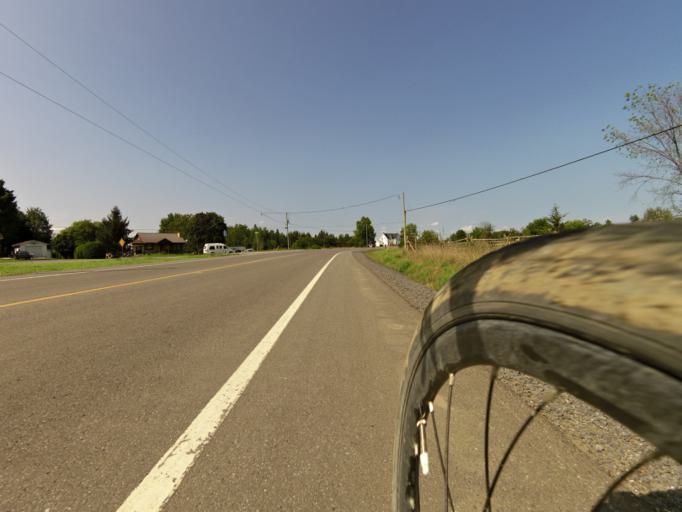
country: CA
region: Ontario
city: Skatepark
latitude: 44.2630
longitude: -76.7240
